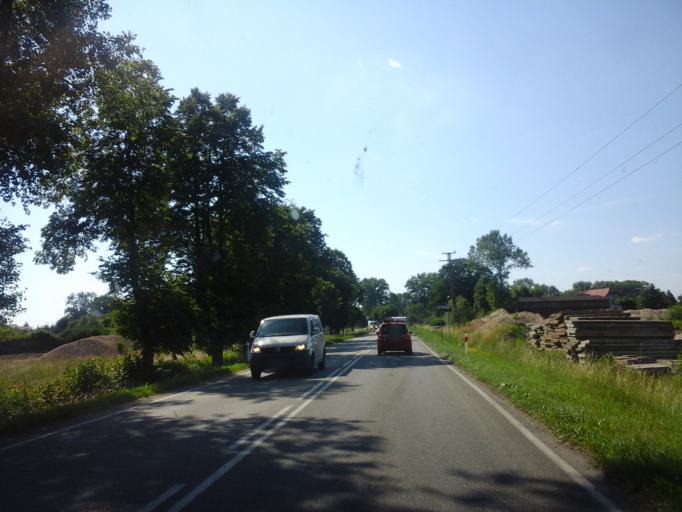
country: PL
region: West Pomeranian Voivodeship
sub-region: Powiat bialogardzki
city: Karlino
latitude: 54.0295
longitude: 15.9048
